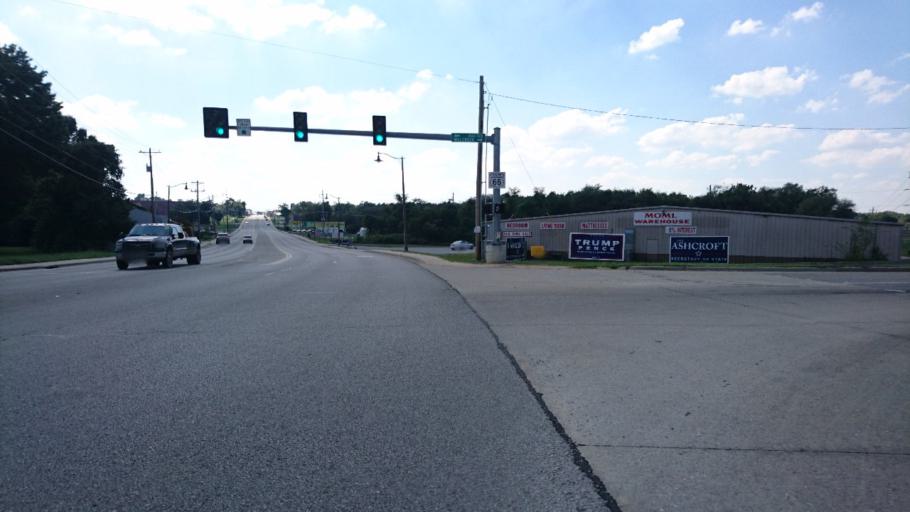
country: US
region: Missouri
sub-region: Laclede County
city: Lebanon
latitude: 37.6837
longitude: -92.6496
